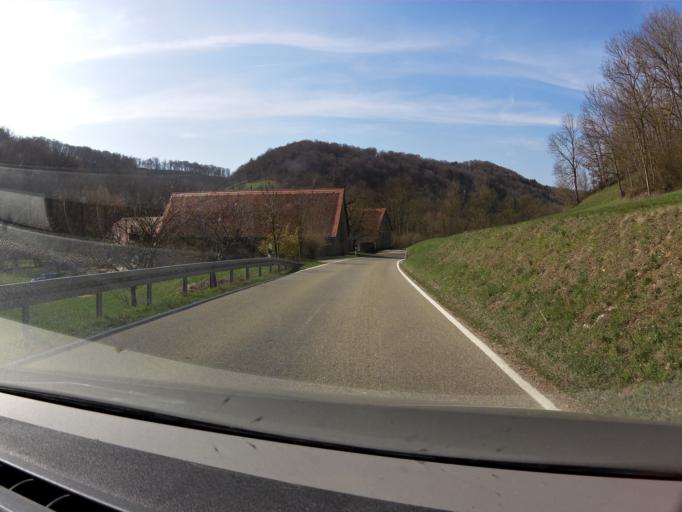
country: DE
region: Bavaria
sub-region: Regierungsbezirk Mittelfranken
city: Rothenburg ob der Tauber
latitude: 49.3991
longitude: 10.1603
